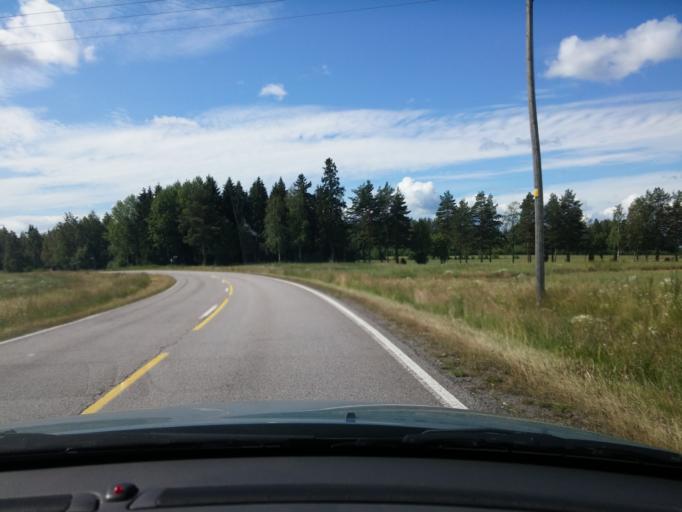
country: FI
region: Uusimaa
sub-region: Porvoo
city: Porvoo
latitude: 60.4065
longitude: 25.6302
